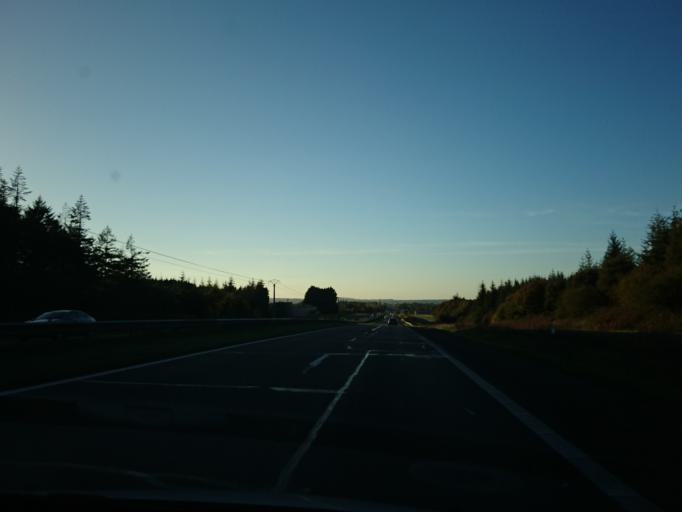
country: FR
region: Brittany
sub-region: Departement des Cotes-d'Armor
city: Lanrodec
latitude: 48.5391
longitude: -3.0650
